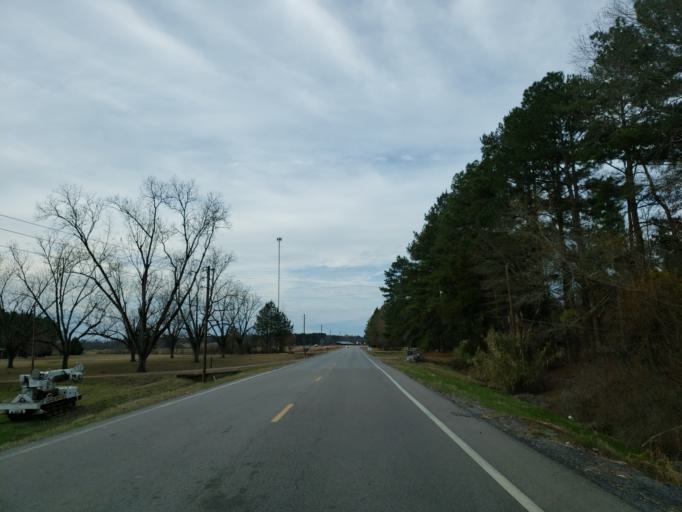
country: US
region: Mississippi
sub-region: Clarke County
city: Quitman
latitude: 31.8759
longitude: -88.7079
